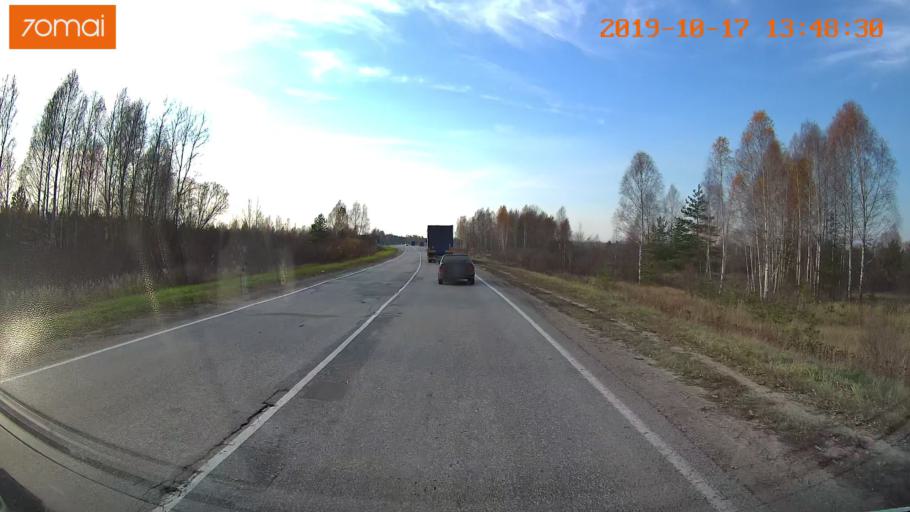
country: RU
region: Rjazan
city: Tuma
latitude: 55.1475
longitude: 40.4552
